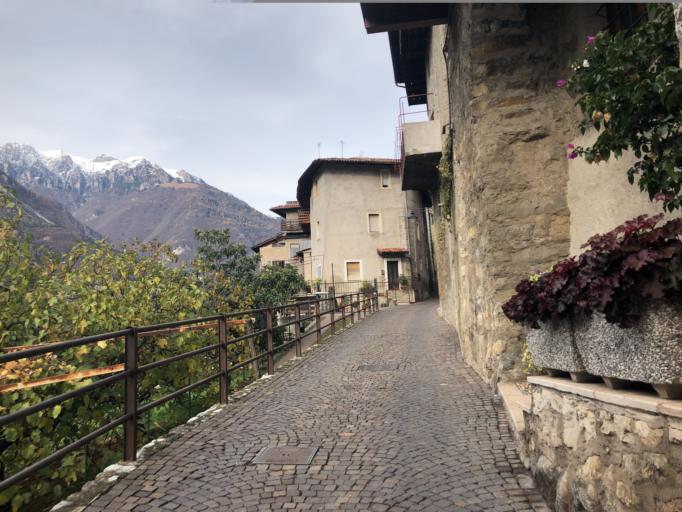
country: IT
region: Trentino-Alto Adige
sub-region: Provincia di Trento
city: Tenno
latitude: 45.9166
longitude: 10.8326
